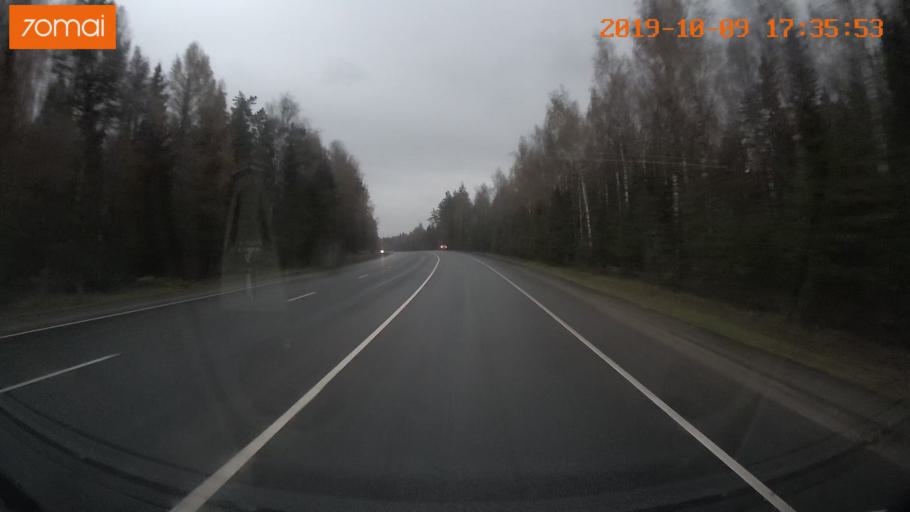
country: RU
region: Ivanovo
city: Bogorodskoye
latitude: 57.0867
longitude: 40.9991
